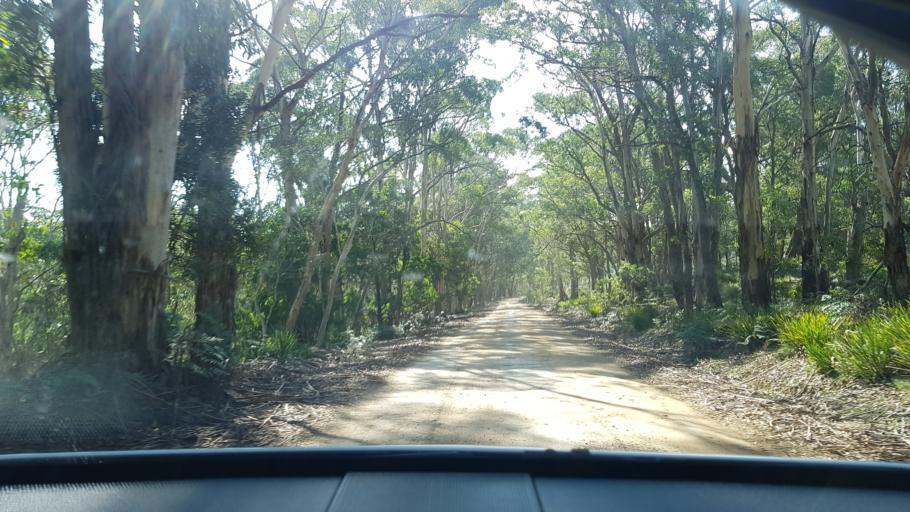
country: AU
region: New South Wales
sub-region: Oberon
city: Oberon
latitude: -33.9793
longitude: 150.0560
